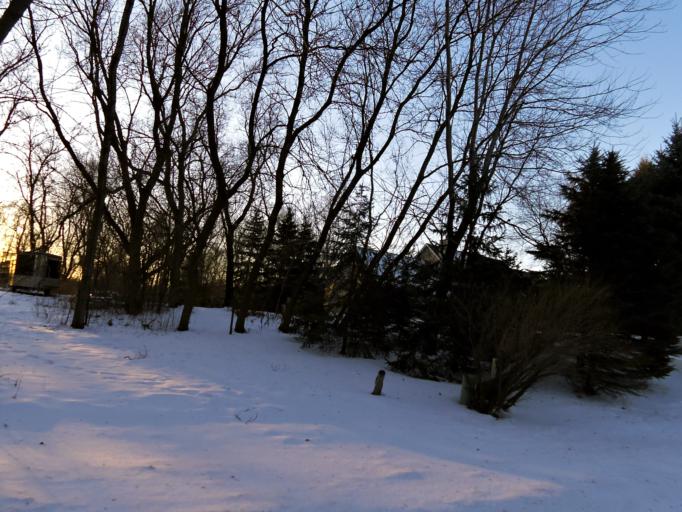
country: US
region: Minnesota
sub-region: Washington County
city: Lakeland
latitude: 44.9644
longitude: -92.8086
